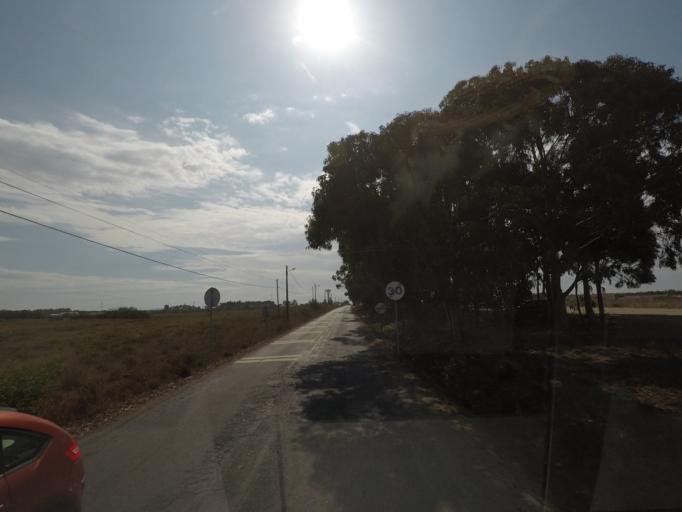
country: PT
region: Beja
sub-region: Odemira
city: Sao Teotonio
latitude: 37.4784
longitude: -8.7641
